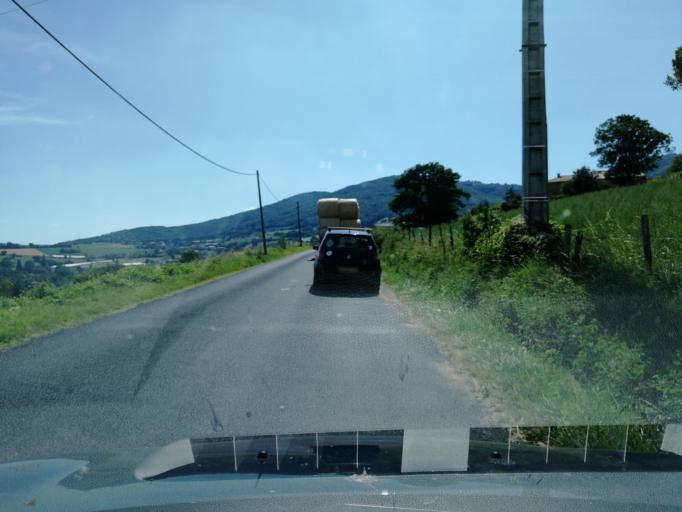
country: FR
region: Rhone-Alpes
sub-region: Departement du Rhone
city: Mornant
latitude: 45.6331
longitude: 4.6336
